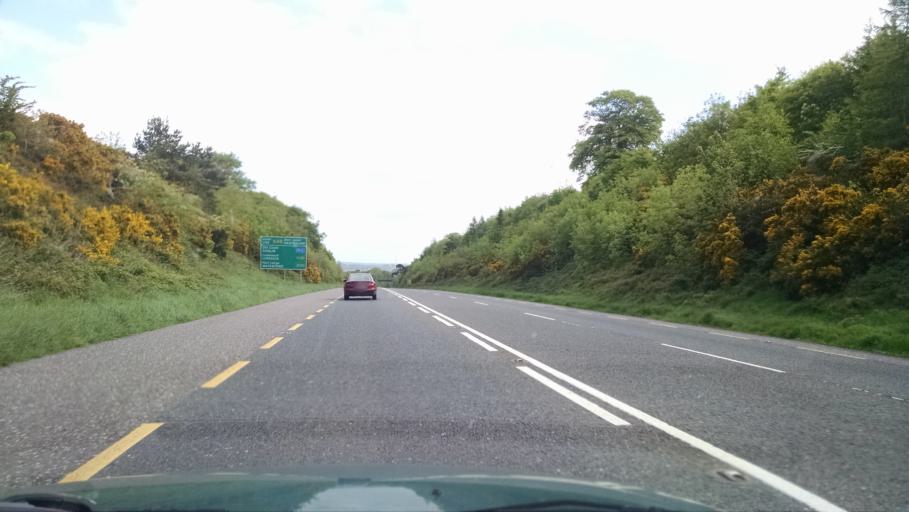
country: IE
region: Munster
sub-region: County Cork
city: Carrigaline
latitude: 51.8635
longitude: -8.4183
